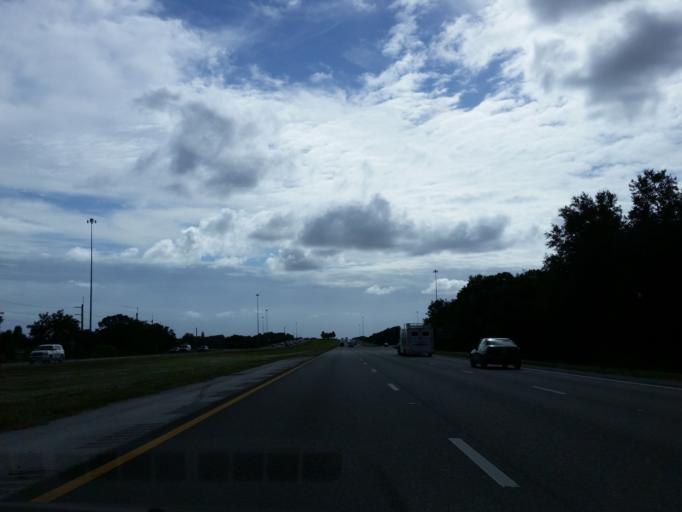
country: US
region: Florida
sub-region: Sarasota County
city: Lake Sarasota
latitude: 27.2762
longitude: -82.4490
